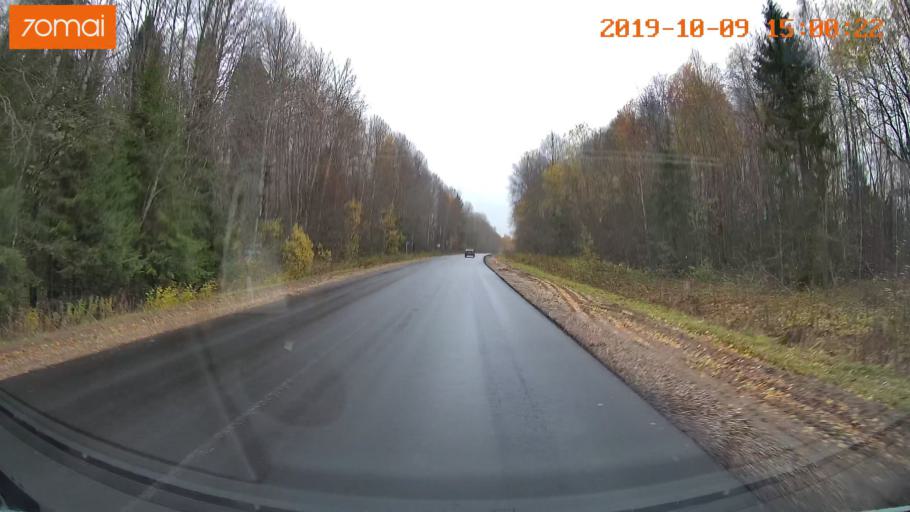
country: RU
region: Kostroma
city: Chistyye Bory
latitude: 58.3100
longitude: 41.6771
